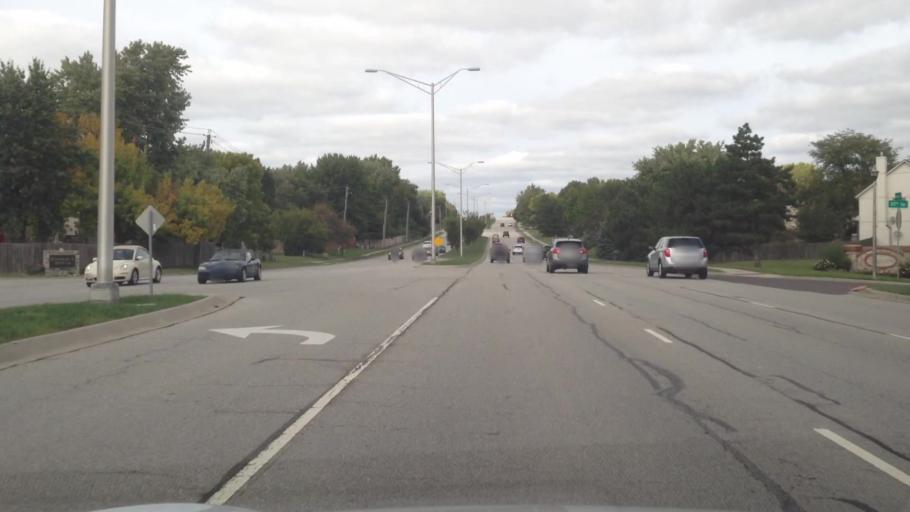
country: US
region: Kansas
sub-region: Johnson County
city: Lenexa
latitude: 38.9151
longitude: -94.7236
